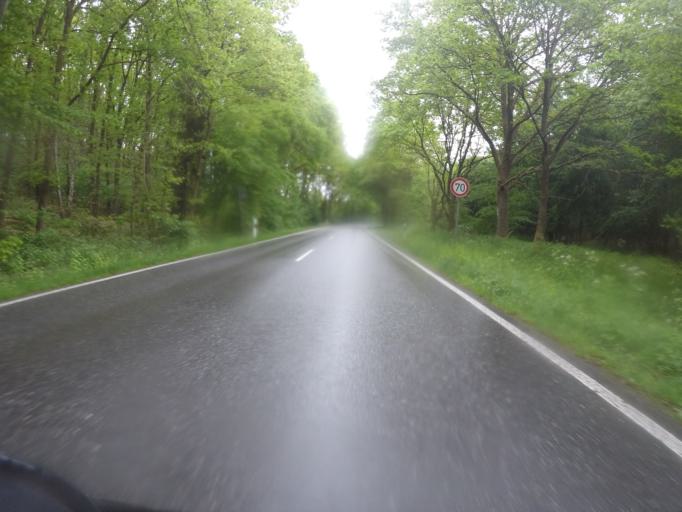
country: DE
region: Schleswig-Holstein
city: Heidmuhlen
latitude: 53.9491
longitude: 10.0850
